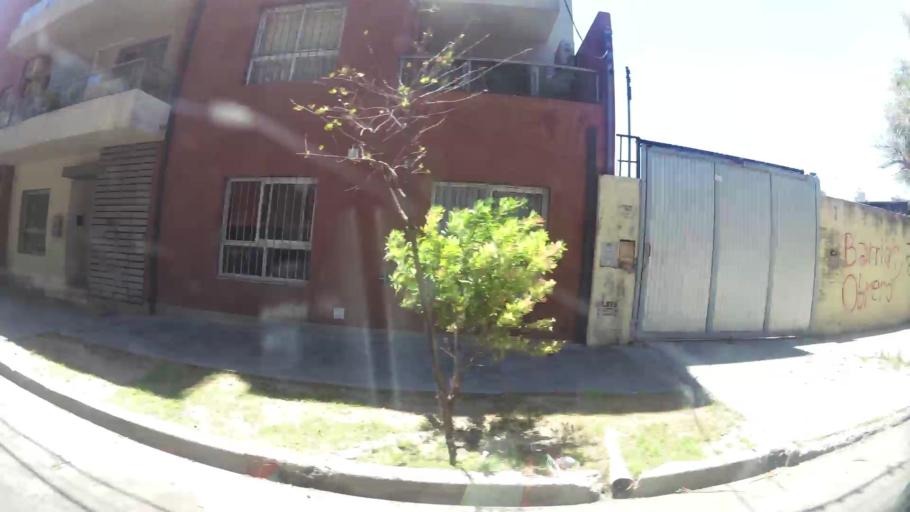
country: AR
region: Cordoba
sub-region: Departamento de Capital
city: Cordoba
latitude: -31.4110
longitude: -64.2128
